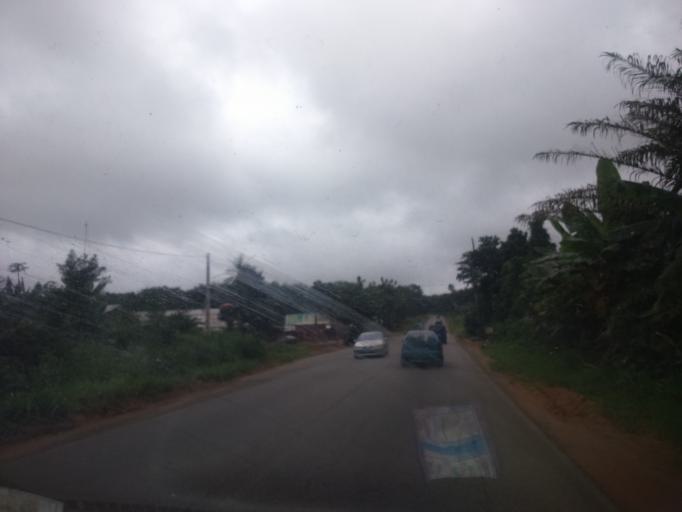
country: CI
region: Sud-Comoe
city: Bonoua
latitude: 5.2814
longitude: -3.5294
